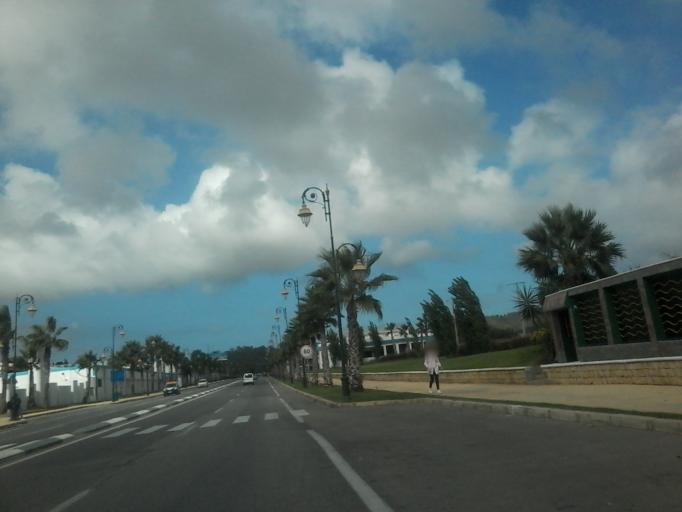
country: MA
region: Tanger-Tetouan
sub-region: Tetouan
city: Martil
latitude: 35.6555
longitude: -5.3192
